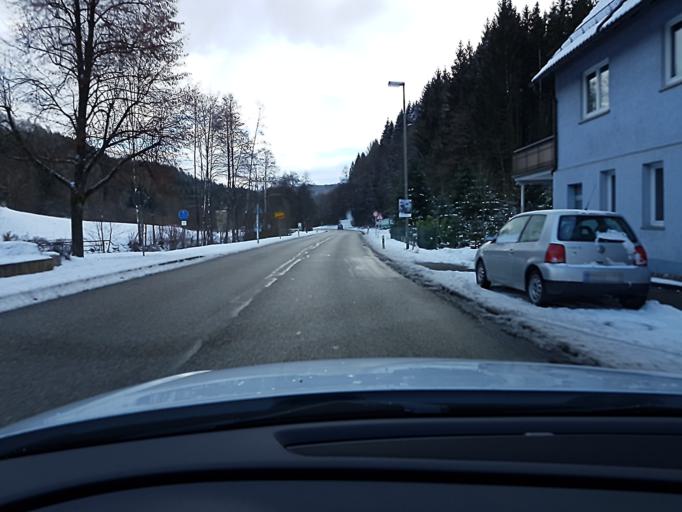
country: DE
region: Baden-Wuerttemberg
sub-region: Regierungsbezirk Stuttgart
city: Spiegelberg
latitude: 49.0341
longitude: 9.4478
